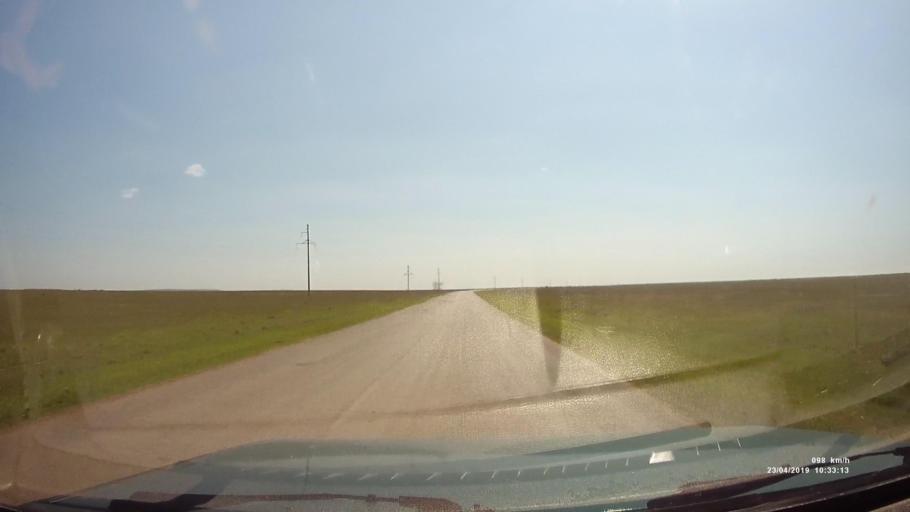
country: RU
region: Kalmykiya
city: Yashalta
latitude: 46.5751
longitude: 42.5925
